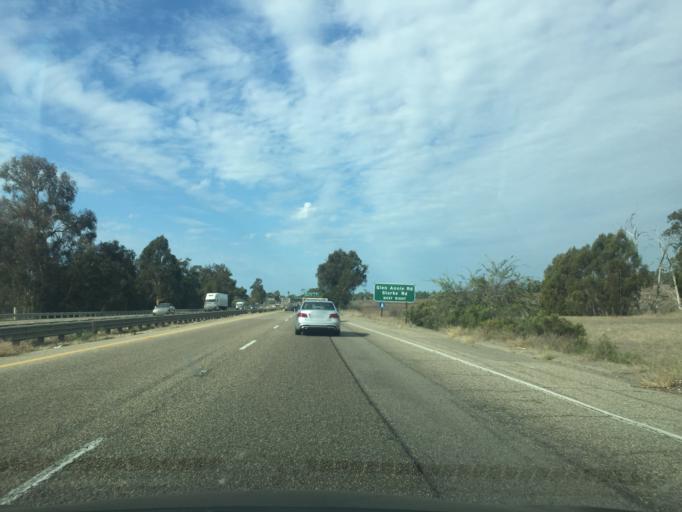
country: US
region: California
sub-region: Santa Barbara County
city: Isla Vista
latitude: 34.4369
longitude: -119.8580
